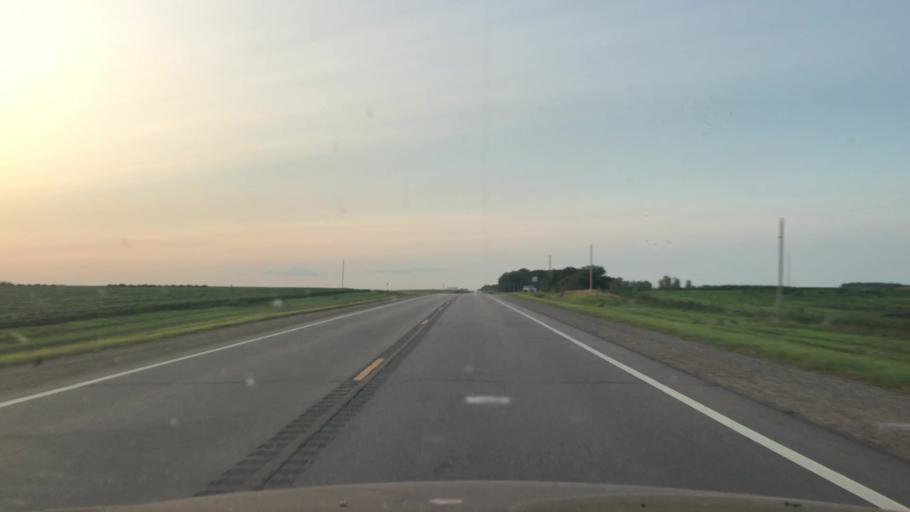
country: US
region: Minnesota
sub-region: Redwood County
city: Redwood Falls
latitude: 44.4395
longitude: -95.1176
